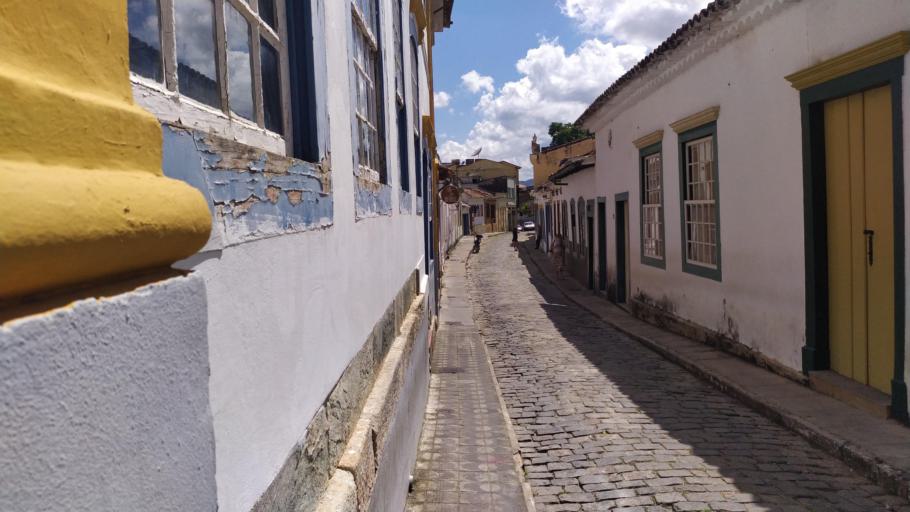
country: BR
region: Minas Gerais
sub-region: Sao Joao Del Rei
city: Sao Joao del Rei
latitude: -21.1338
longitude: -44.2606
